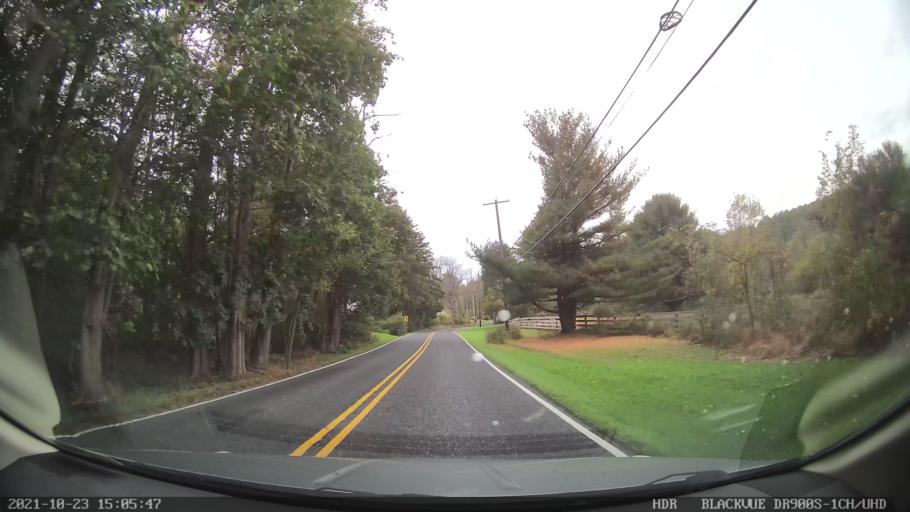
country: US
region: Pennsylvania
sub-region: Berks County
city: Bally
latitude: 40.4337
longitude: -75.5841
